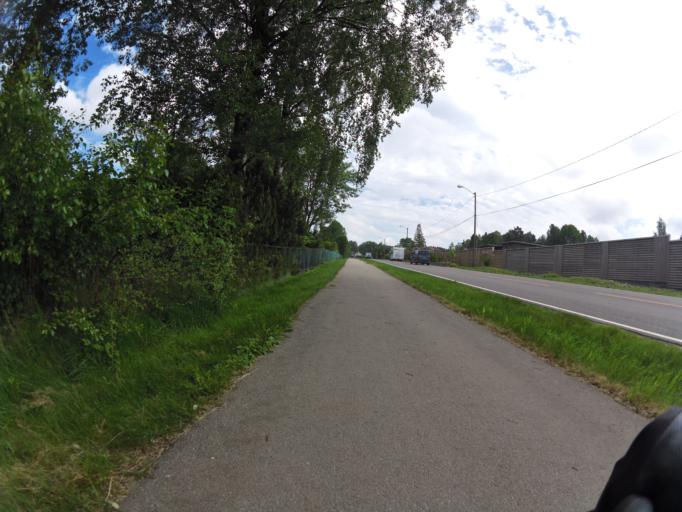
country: NO
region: Ostfold
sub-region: Rygge
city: Ryggebyen
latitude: 59.3734
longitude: 10.7705
